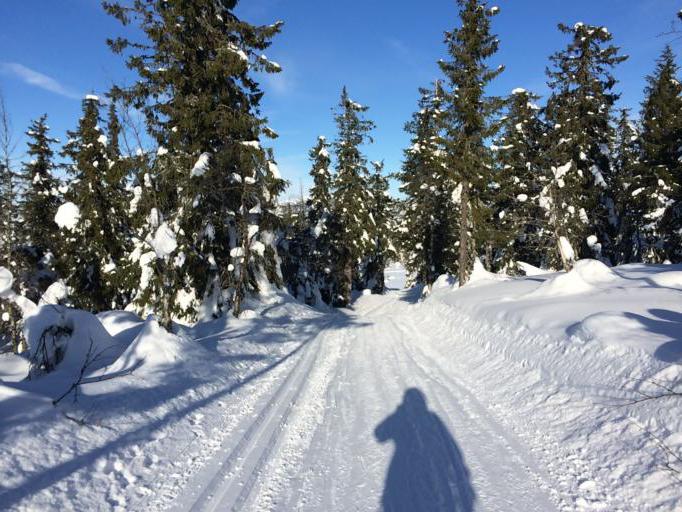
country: NO
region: Oppland
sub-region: Gausdal
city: Segalstad bru
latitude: 61.3125
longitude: 10.1046
